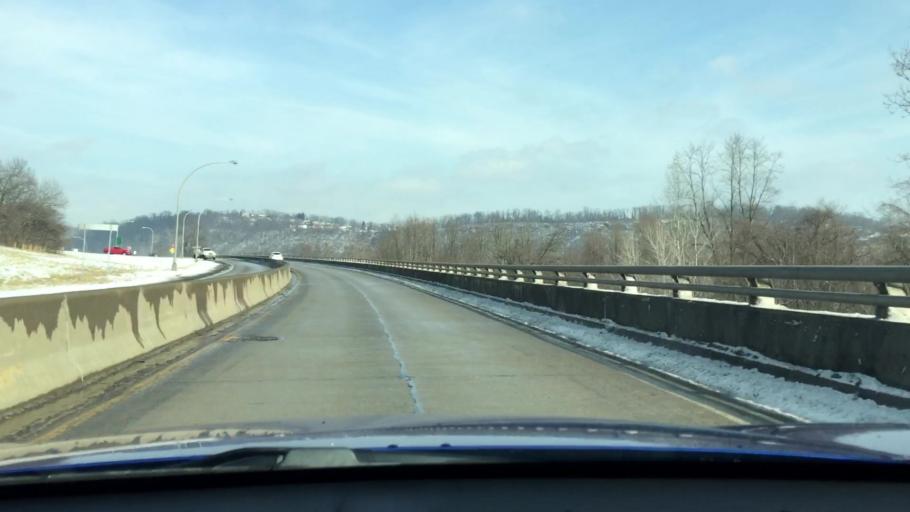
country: US
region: Pennsylvania
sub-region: Allegheny County
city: West Mifflin
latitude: 40.3607
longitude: -79.8447
